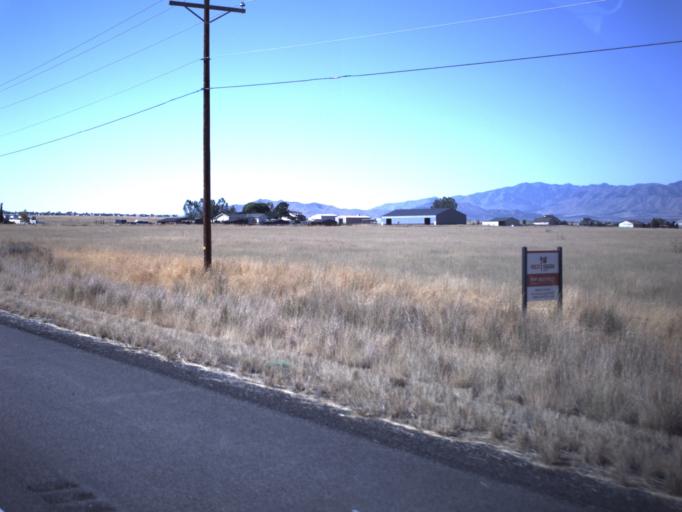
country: US
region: Utah
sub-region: Tooele County
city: Erda
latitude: 40.5979
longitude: -112.2942
